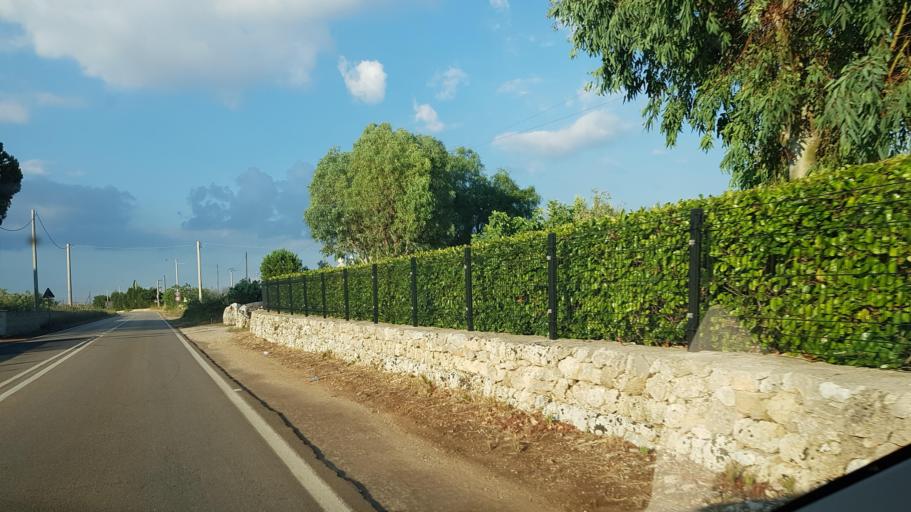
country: IT
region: Apulia
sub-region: Provincia di Lecce
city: Acquarica del Capo
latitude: 39.8680
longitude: 18.2175
